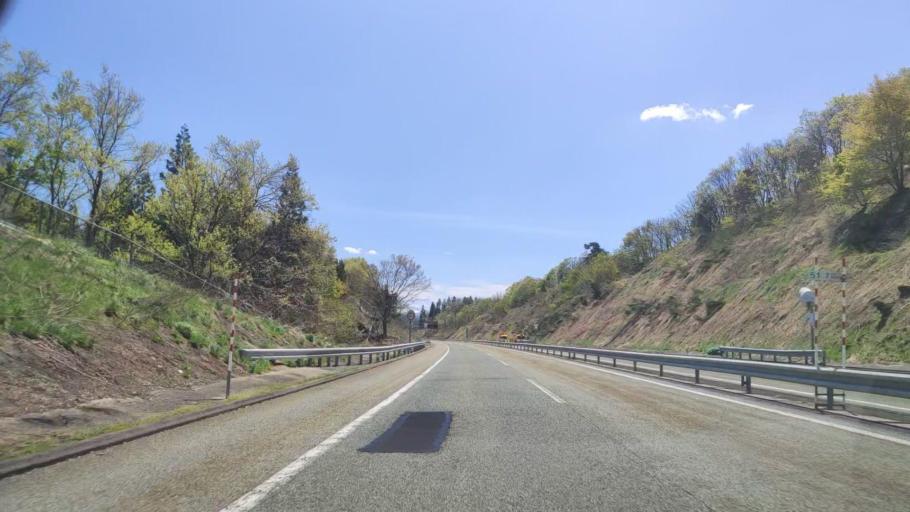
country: JP
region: Akita
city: Yokotemachi
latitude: 39.2829
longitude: 140.5337
